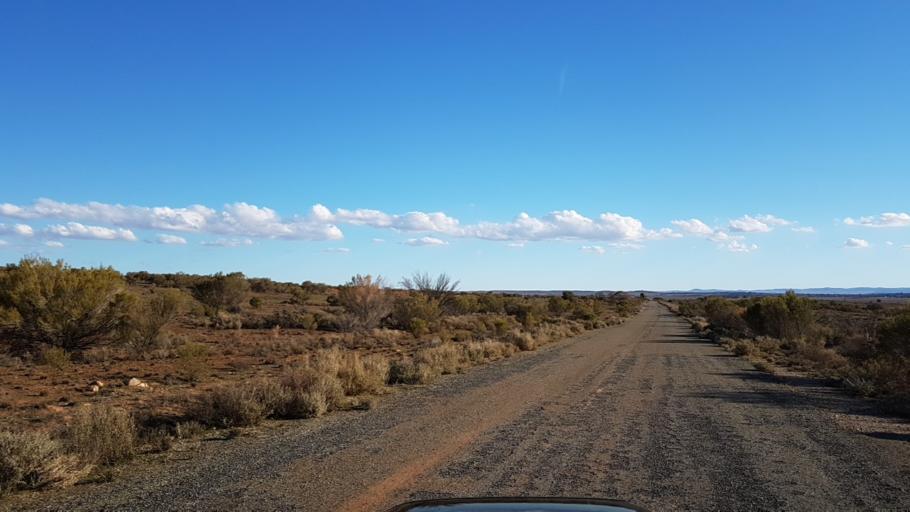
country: AU
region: South Australia
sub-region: Peterborough
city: Peterborough
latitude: -32.9552
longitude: 138.9026
